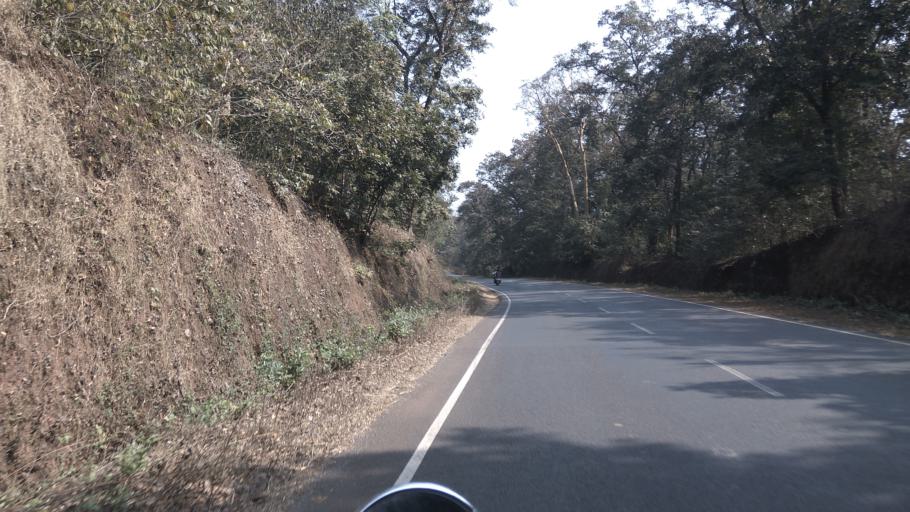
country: IN
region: Goa
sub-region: South Goa
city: Sanvordem
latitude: 15.3618
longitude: 74.1991
